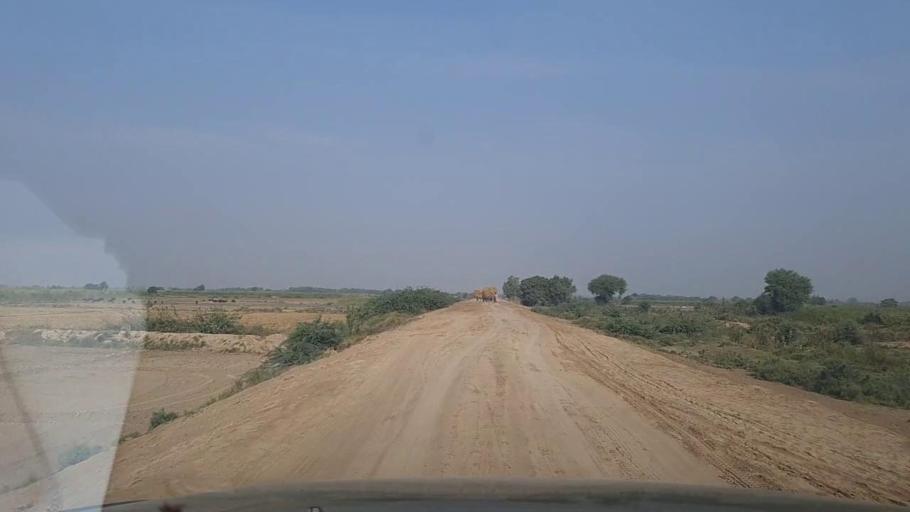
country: PK
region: Sindh
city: Bulri
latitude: 24.9956
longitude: 68.2908
